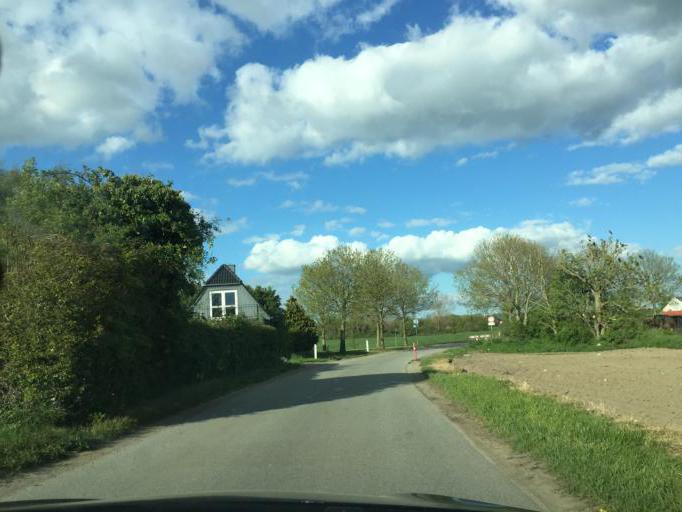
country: DK
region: South Denmark
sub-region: Odense Kommune
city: Bellinge
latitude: 55.3688
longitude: 10.2967
